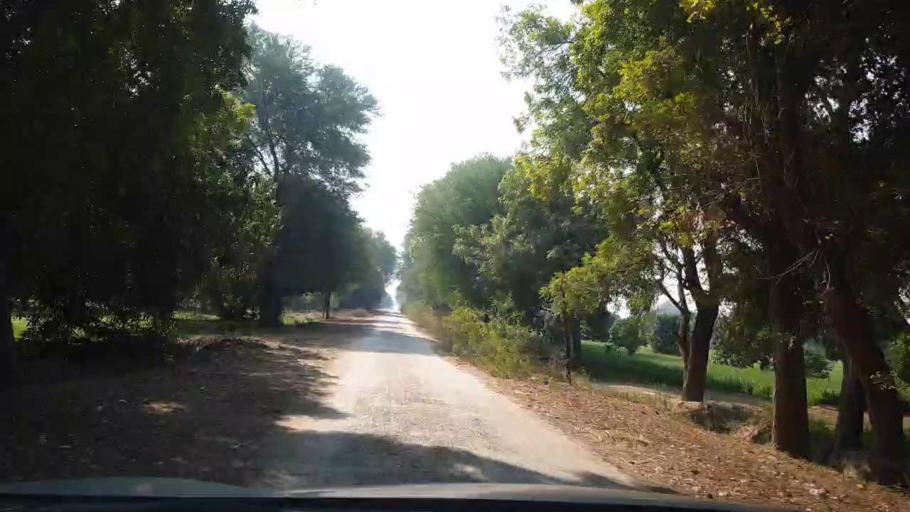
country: PK
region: Sindh
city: Tando Allahyar
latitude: 25.5182
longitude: 68.7861
